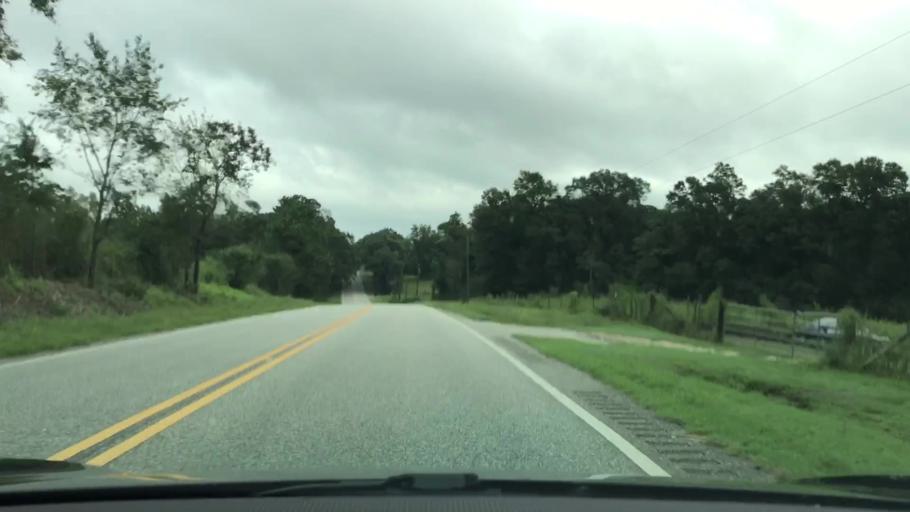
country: US
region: Alabama
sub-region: Geneva County
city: Samson
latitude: 31.0267
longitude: -86.1147
